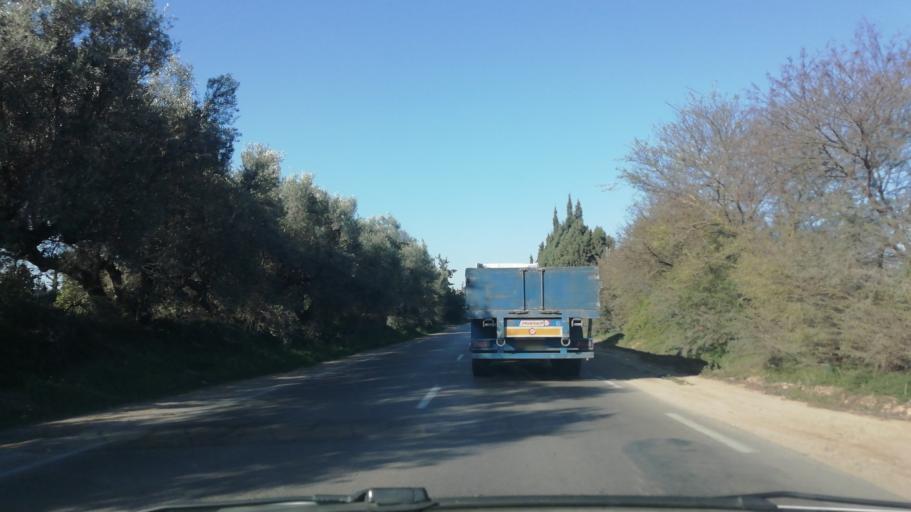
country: DZ
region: Mascara
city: Sig
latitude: 35.5740
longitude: -0.0132
